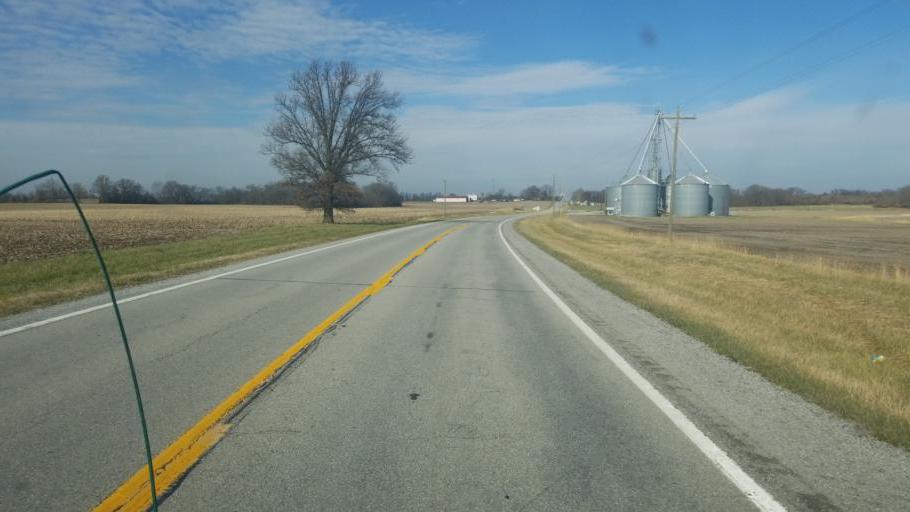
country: US
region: Illinois
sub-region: Saline County
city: Eldorado
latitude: 37.9164
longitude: -88.4575
